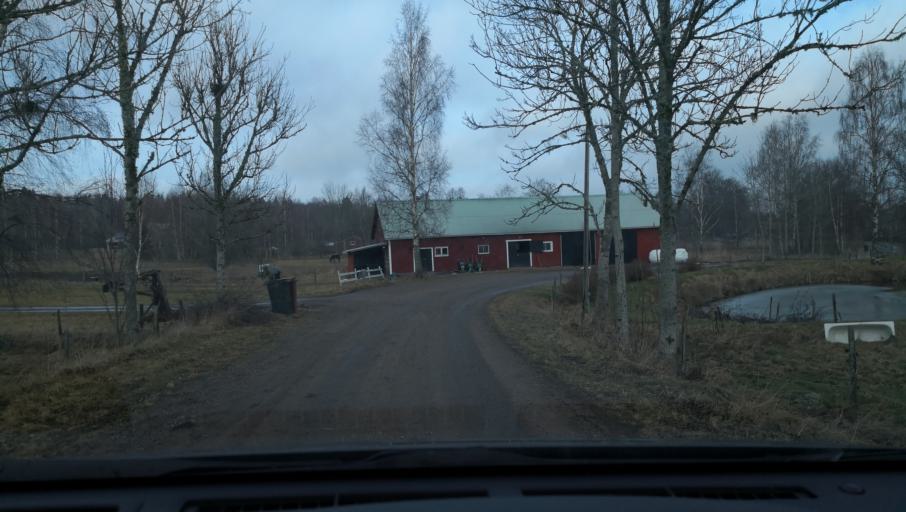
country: SE
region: Vaestra Goetaland
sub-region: Gullspangs Kommun
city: Gullspang
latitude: 58.9607
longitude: 14.0902
